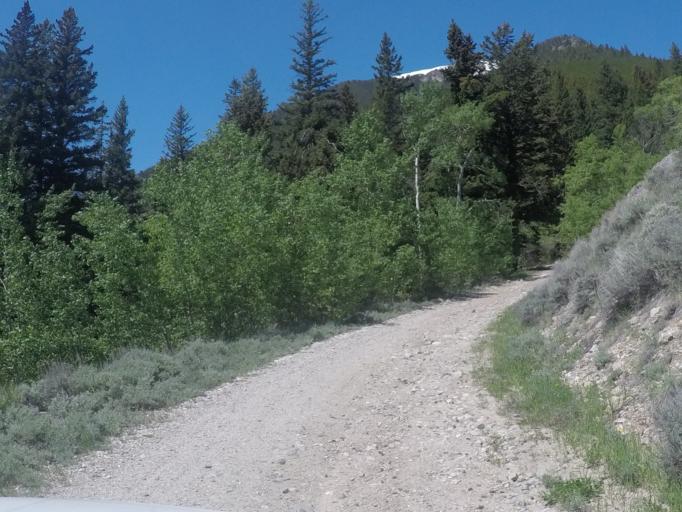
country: US
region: Montana
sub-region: Carbon County
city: Red Lodge
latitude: 45.0574
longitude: -109.4228
